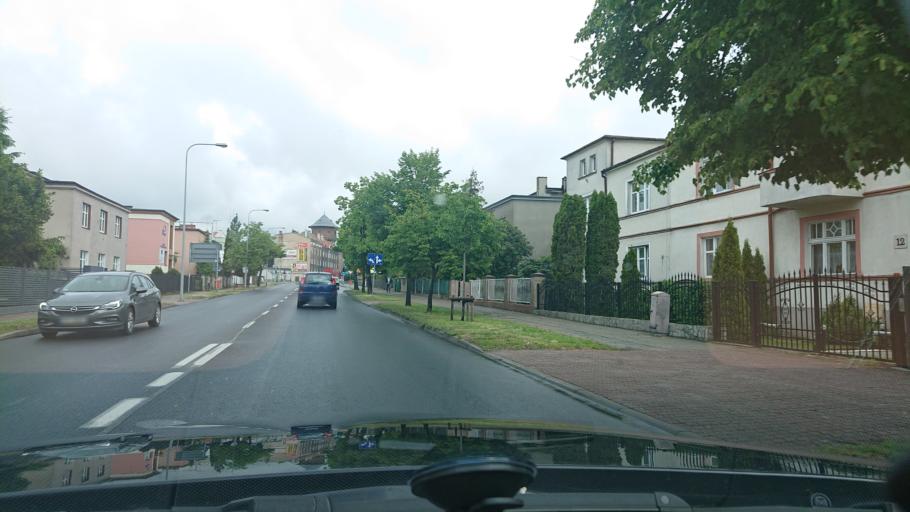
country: PL
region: Greater Poland Voivodeship
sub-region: Powiat gnieznienski
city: Gniezno
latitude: 52.5393
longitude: 17.6069
